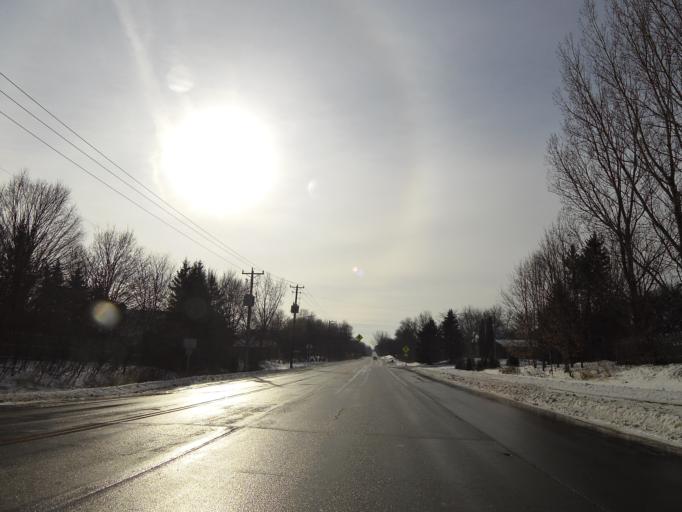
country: US
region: Minnesota
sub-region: Carver County
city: Chanhassen
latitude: 44.8887
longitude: -93.5206
